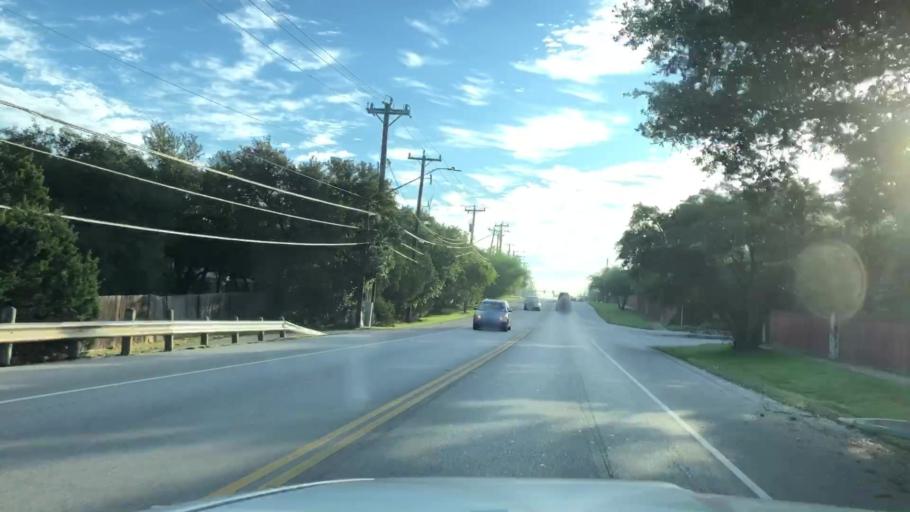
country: US
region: Texas
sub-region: Bexar County
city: Leon Valley
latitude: 29.5444
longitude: -98.6435
